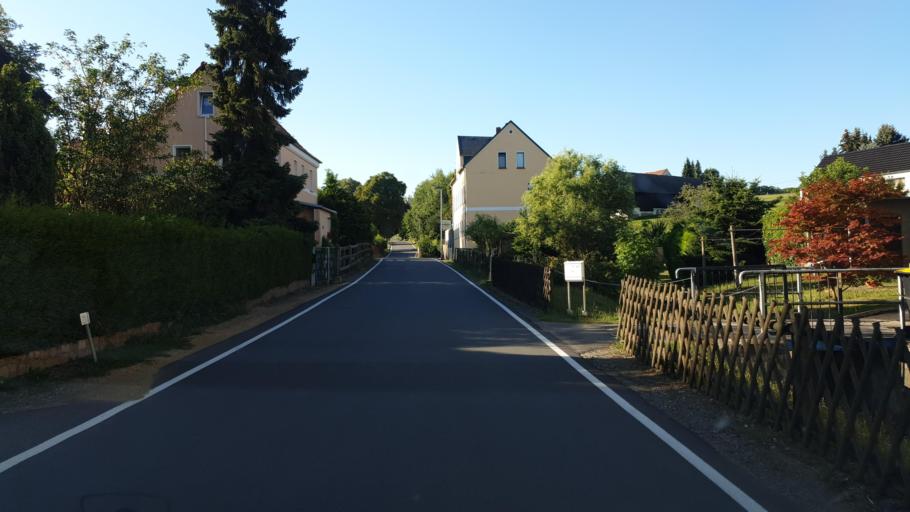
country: DE
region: Saxony
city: Lichtentanne
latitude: 50.6721
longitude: 12.4311
